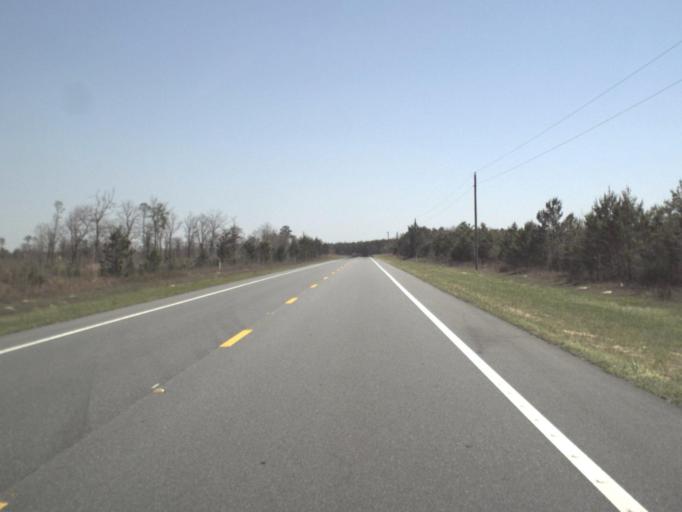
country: US
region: Florida
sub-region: Bay County
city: Youngstown
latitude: 30.4262
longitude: -85.3188
